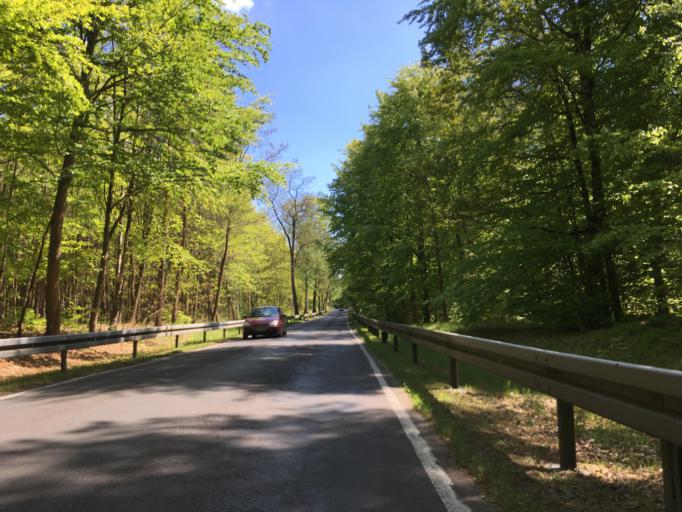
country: DE
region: Brandenburg
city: Bernau bei Berlin
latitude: 52.7166
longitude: 13.5742
